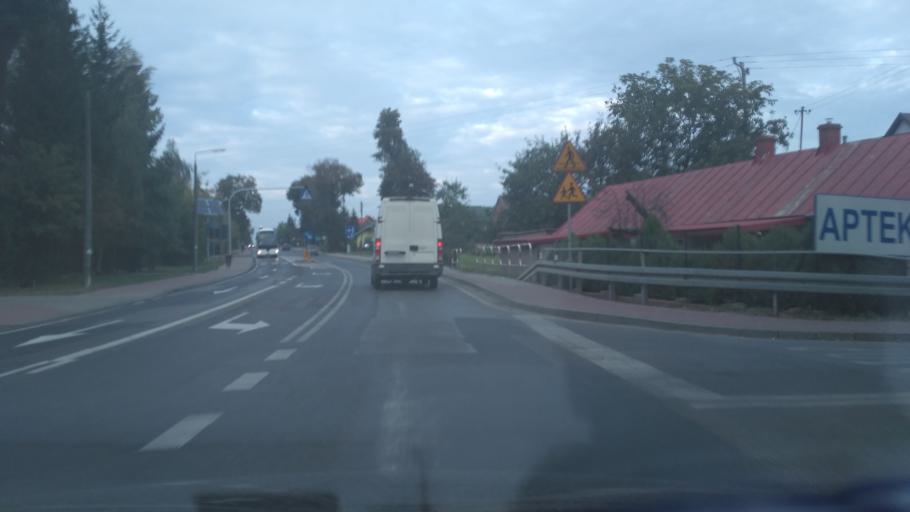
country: PL
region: Lublin Voivodeship
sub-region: Powiat lubelski
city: Jakubowice Murowane
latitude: 51.2648
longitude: 22.6332
